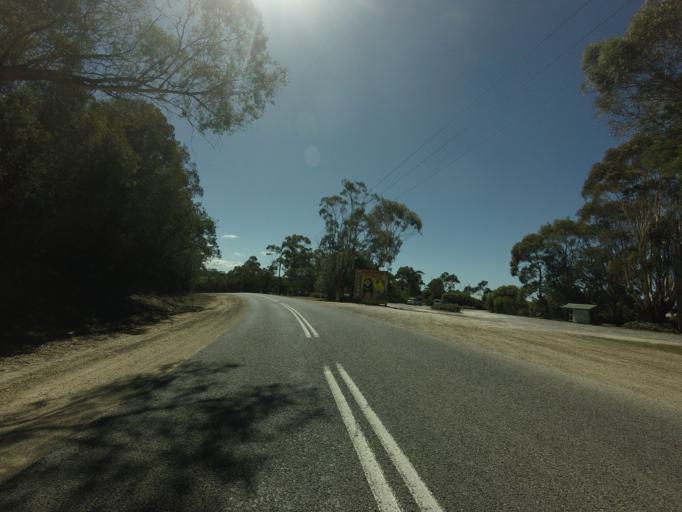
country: AU
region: Tasmania
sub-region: Break O'Day
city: St Helens
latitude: -41.8382
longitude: 148.2551
